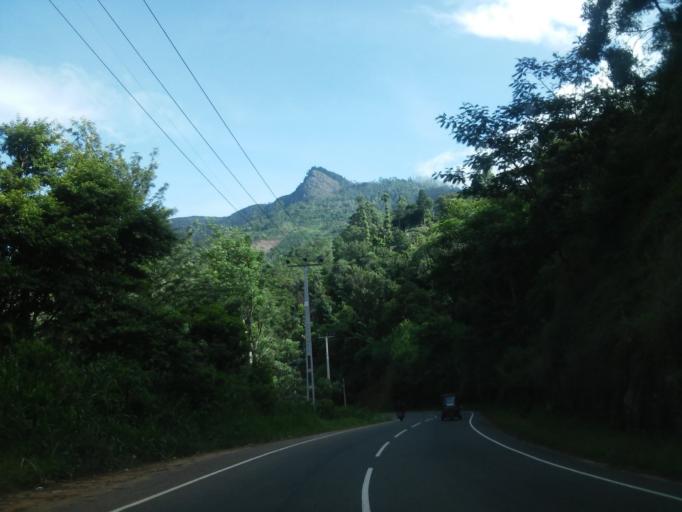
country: LK
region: Uva
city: Haputale
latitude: 6.7632
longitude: 80.8997
